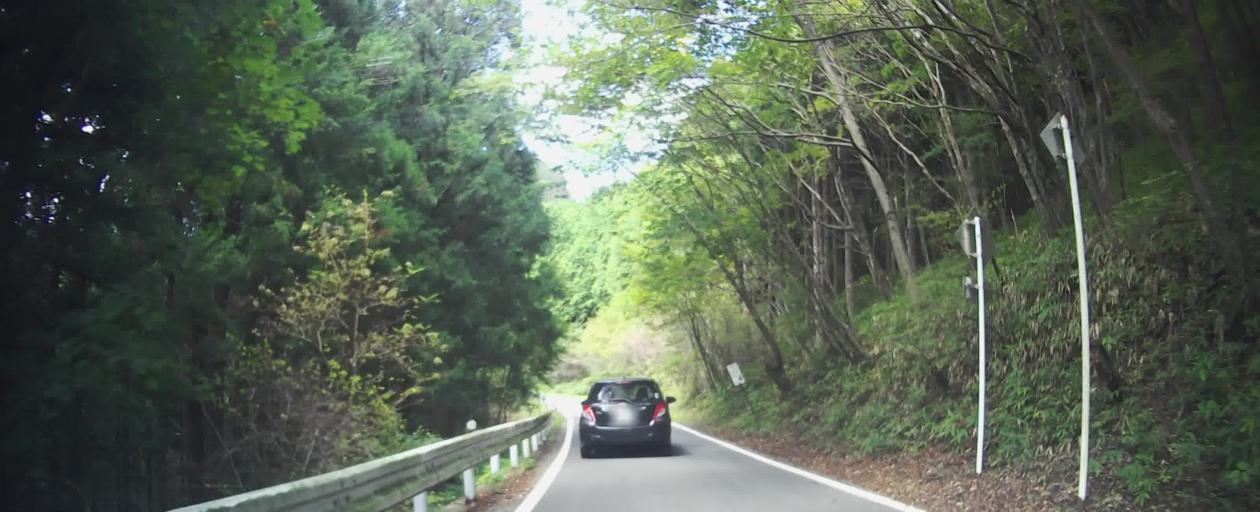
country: JP
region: Gunma
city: Shibukawa
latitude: 36.4631
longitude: 138.8905
